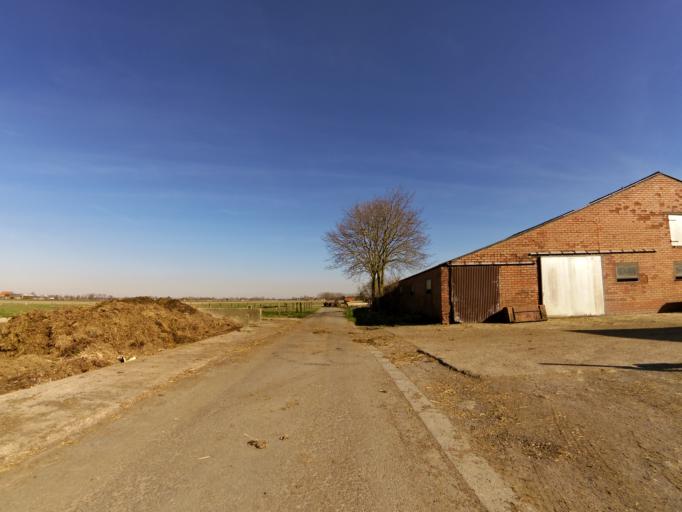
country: BE
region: Flanders
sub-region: Provincie West-Vlaanderen
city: Ostend
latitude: 51.1921
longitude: 2.9456
